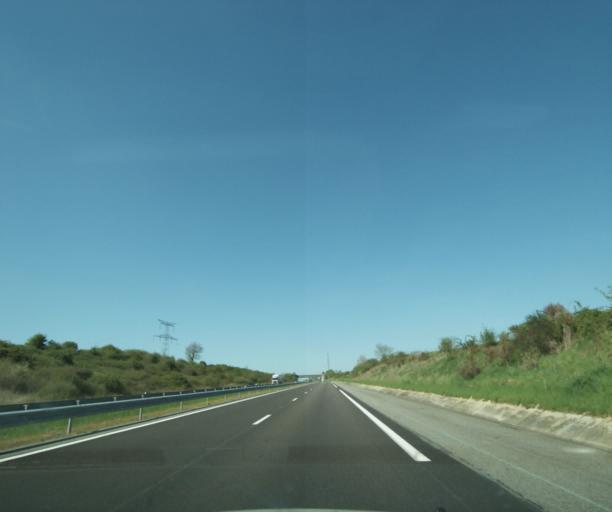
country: FR
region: Bourgogne
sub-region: Departement de la Nievre
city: Cosne-Cours-sur-Loire
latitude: 47.4546
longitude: 2.9480
